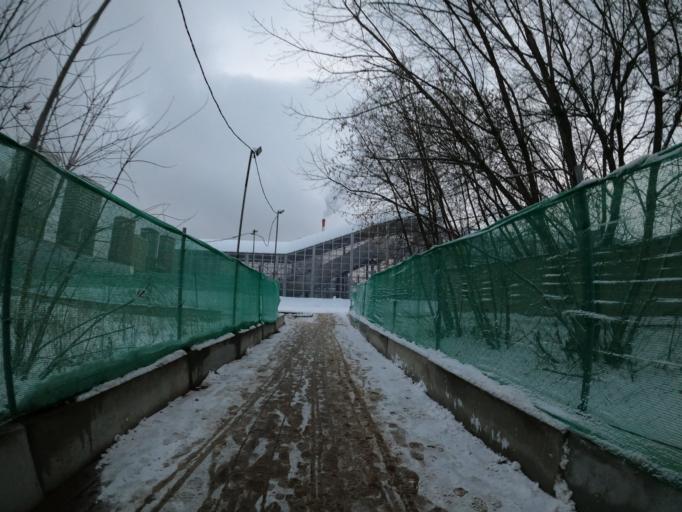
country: RU
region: Moskovskaya
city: Kur'yanovo
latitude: 55.6492
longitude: 37.7041
